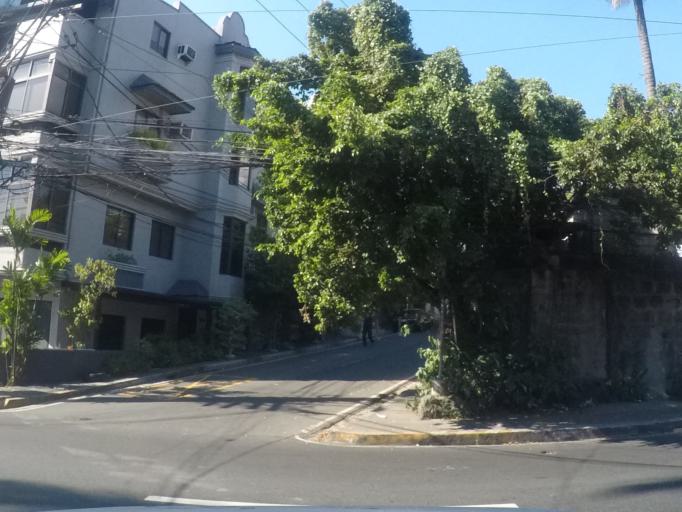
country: PH
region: Metro Manila
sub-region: San Juan
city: San Juan
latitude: 14.6089
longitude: 121.0310
